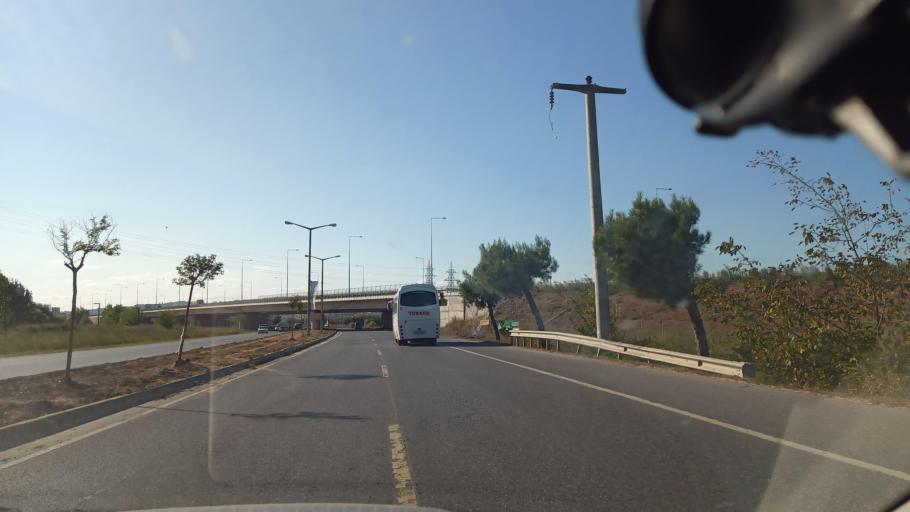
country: TR
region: Sakarya
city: Kazimpasa
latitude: 40.8431
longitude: 30.3348
